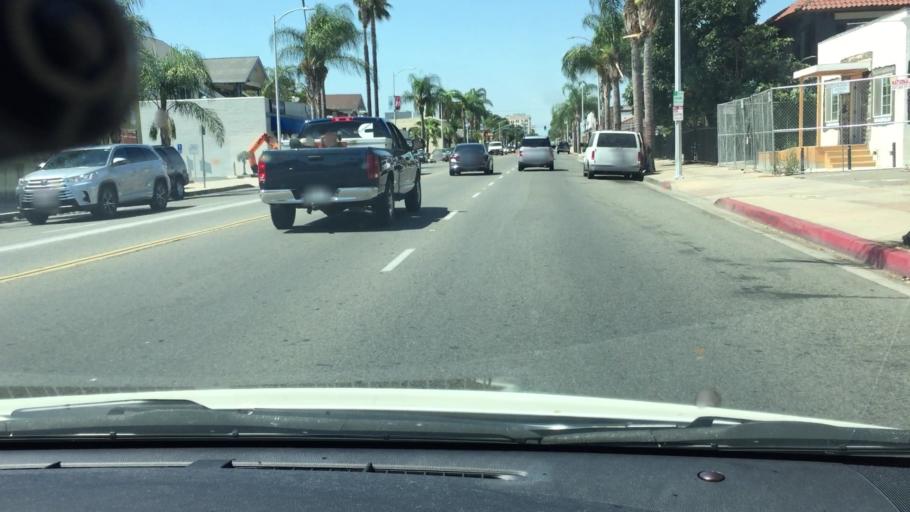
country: US
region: California
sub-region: Orange County
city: Santa Ana
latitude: 33.7401
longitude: -117.8676
